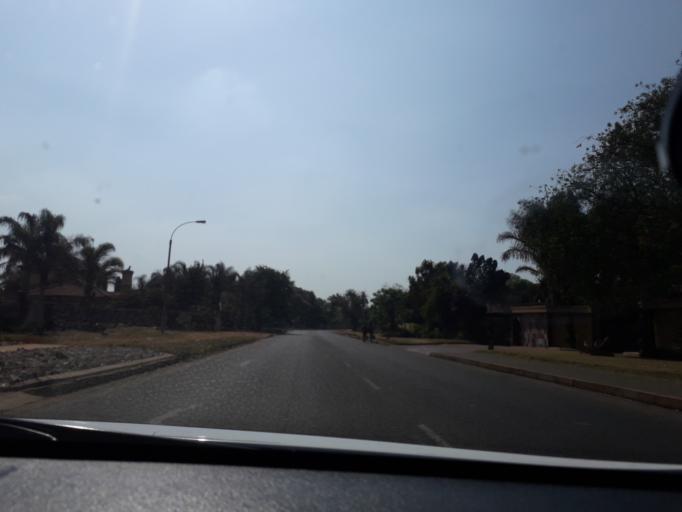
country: ZA
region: Gauteng
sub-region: City of Johannesburg Metropolitan Municipality
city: Modderfontein
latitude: -26.0806
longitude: 28.2394
